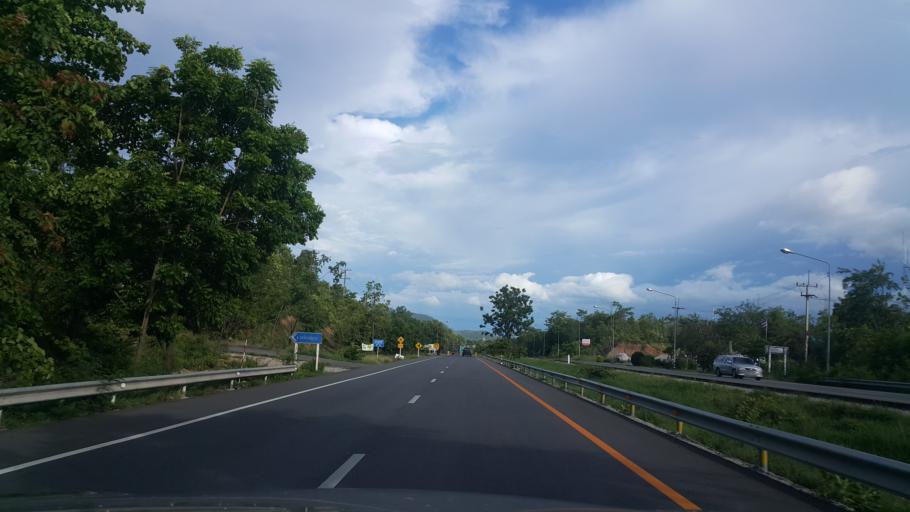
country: TH
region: Tak
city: Ban Tak
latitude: 17.0419
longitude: 99.0829
